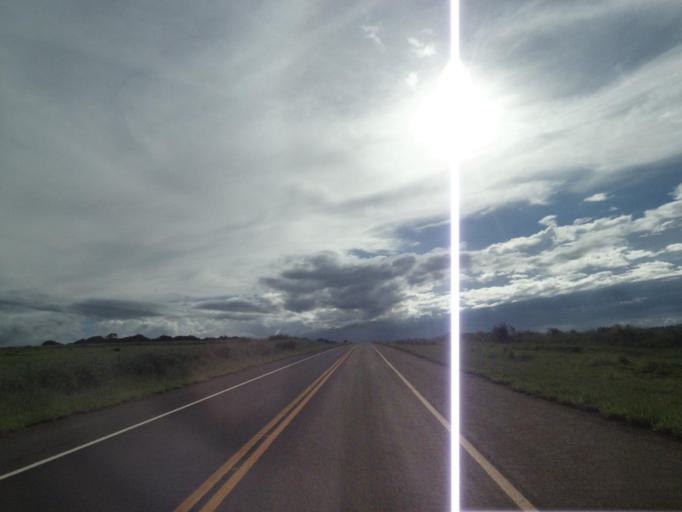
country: BR
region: Goias
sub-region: Jaragua
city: Jaragua
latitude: -15.8998
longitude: -49.5289
